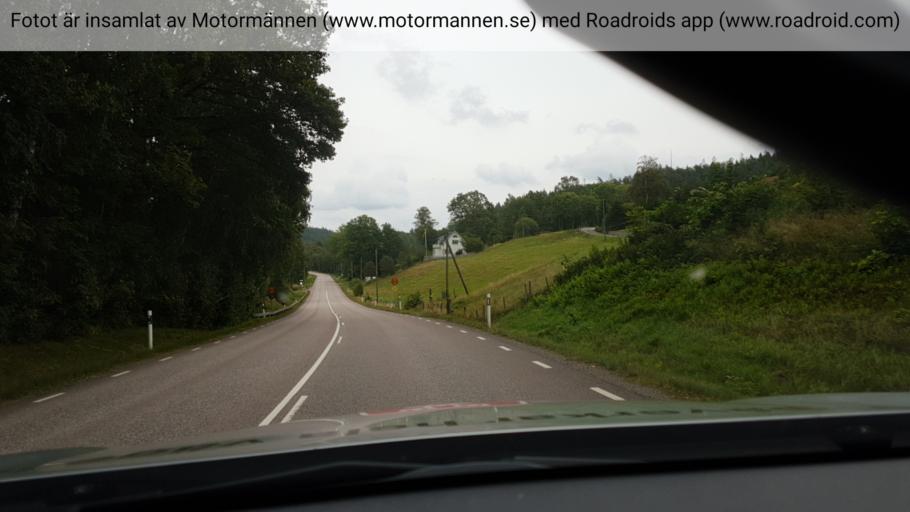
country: SE
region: Vaestra Goetaland
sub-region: Harryda Kommun
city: Landvetter
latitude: 57.6011
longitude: 12.2034
